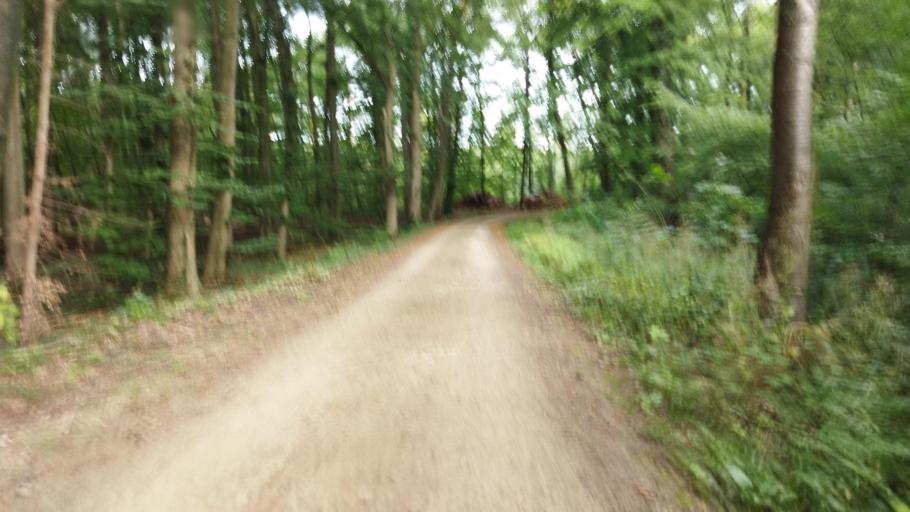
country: DE
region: Lower Saxony
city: Bad Rothenfelde
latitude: 52.0889
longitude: 8.1583
